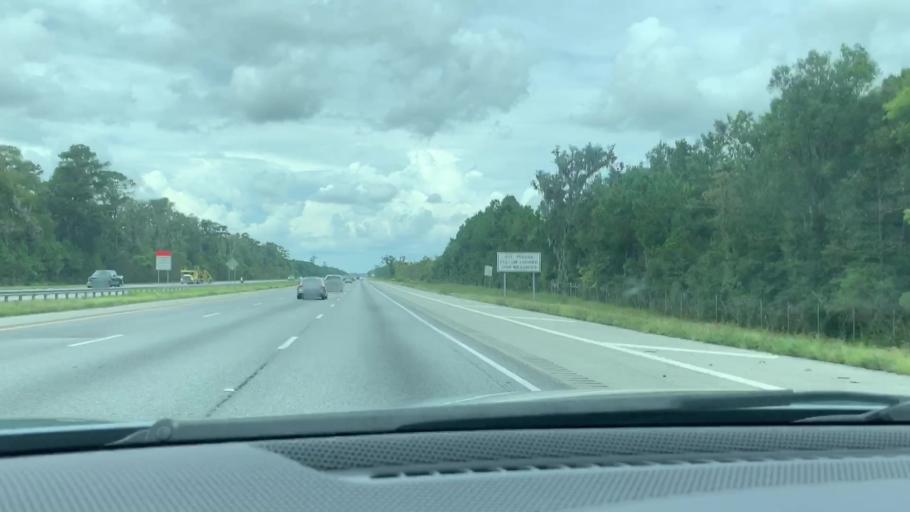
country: US
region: Georgia
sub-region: McIntosh County
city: Darien
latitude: 31.4421
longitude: -81.4444
